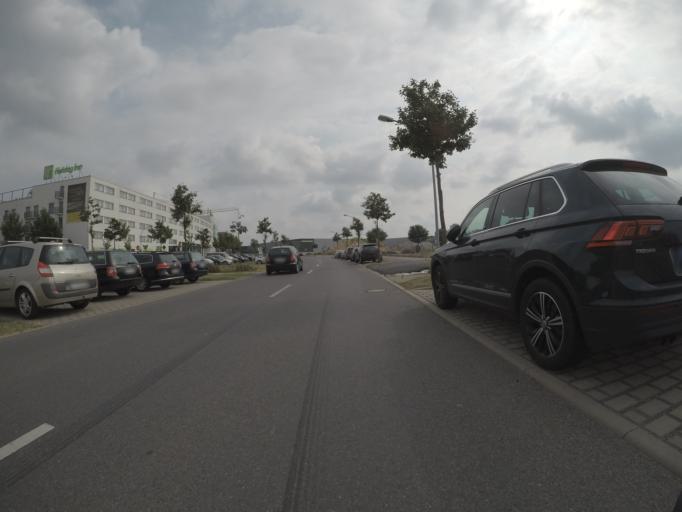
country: DE
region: Brandenburg
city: Schonefeld
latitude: 52.3899
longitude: 13.4979
